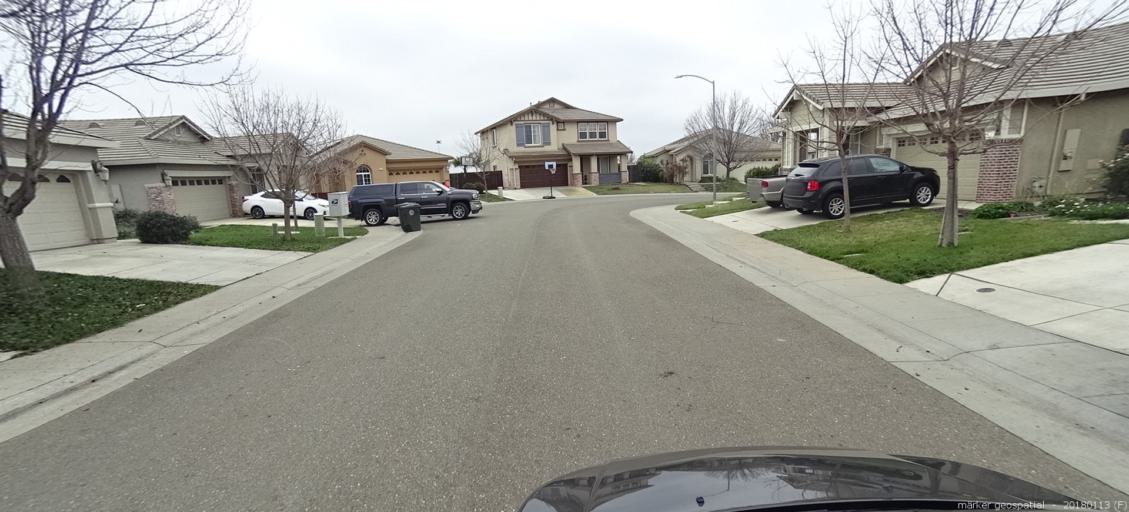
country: US
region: California
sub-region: Sacramento County
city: Gold River
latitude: 38.5522
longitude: -121.2187
